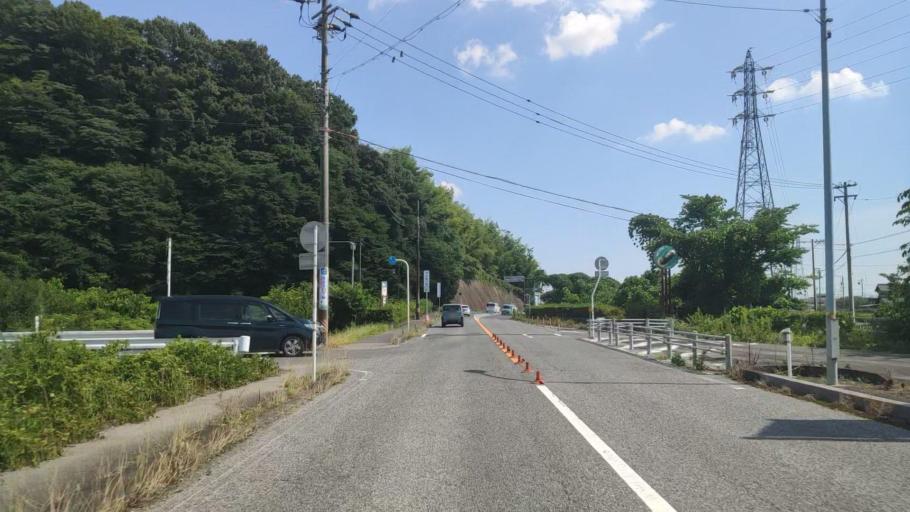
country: JP
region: Gifu
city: Godo
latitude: 35.4752
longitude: 136.6759
